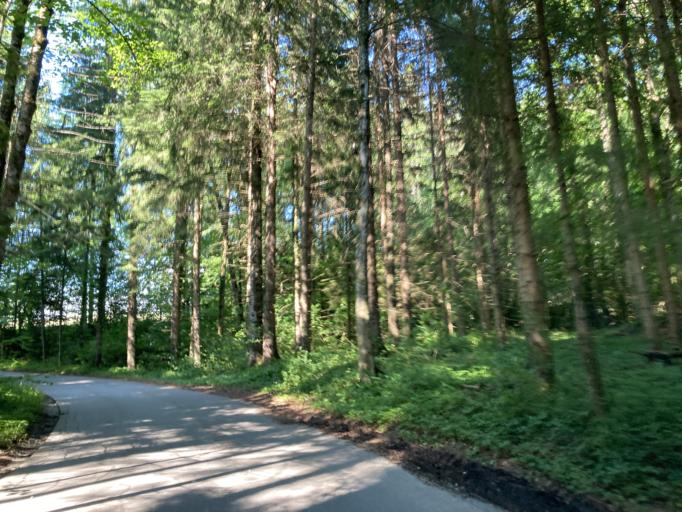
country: DE
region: Bavaria
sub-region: Upper Bavaria
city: Samerberg
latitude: 47.7536
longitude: 12.2036
